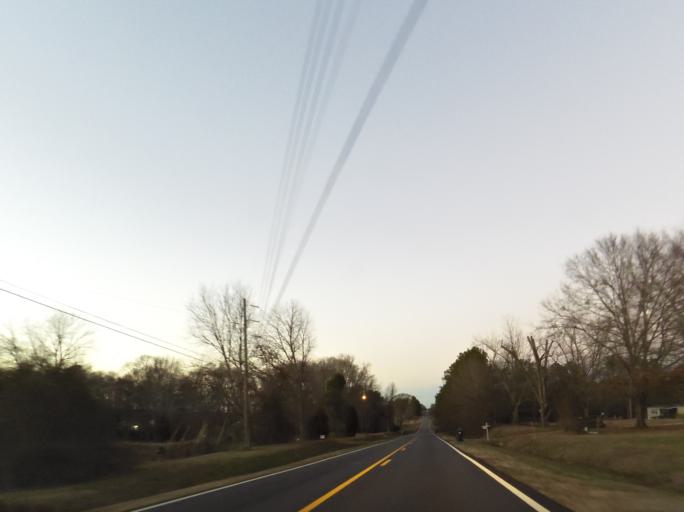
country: US
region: Georgia
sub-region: Peach County
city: Byron
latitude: 32.6240
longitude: -83.7574
